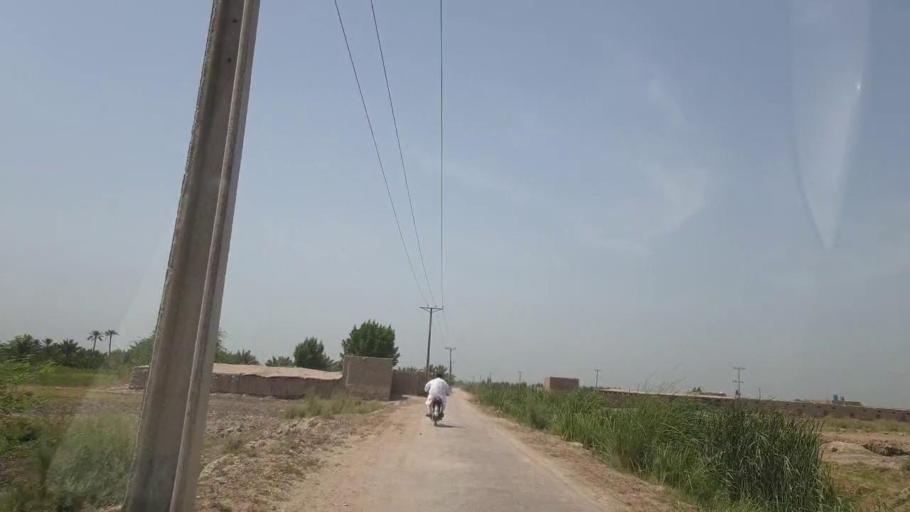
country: PK
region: Sindh
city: Ranipur
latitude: 27.3093
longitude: 68.5473
